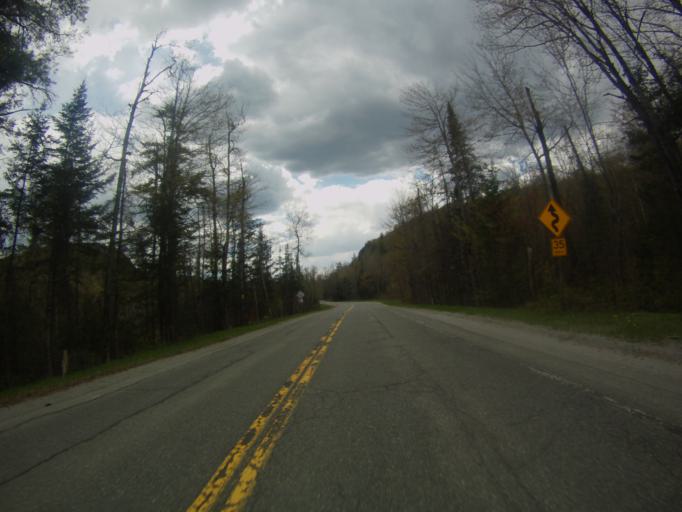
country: US
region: New York
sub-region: Essex County
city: Mineville
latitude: 44.0992
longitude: -73.5701
